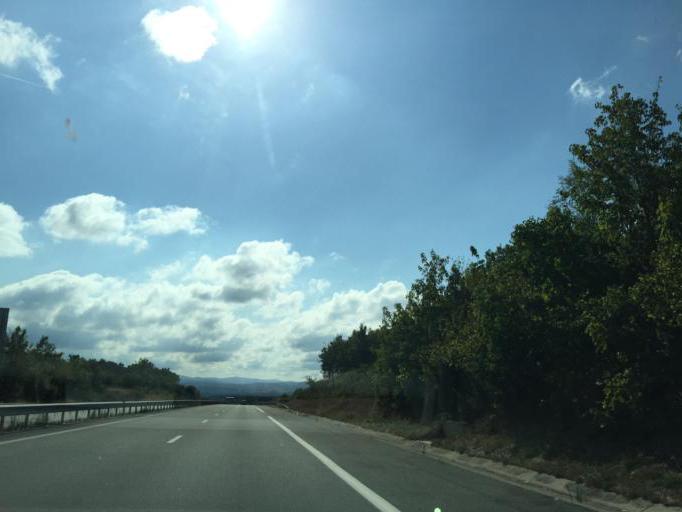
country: FR
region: Rhone-Alpes
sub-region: Departement de la Loire
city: Balbigny
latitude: 45.8250
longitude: 4.1345
